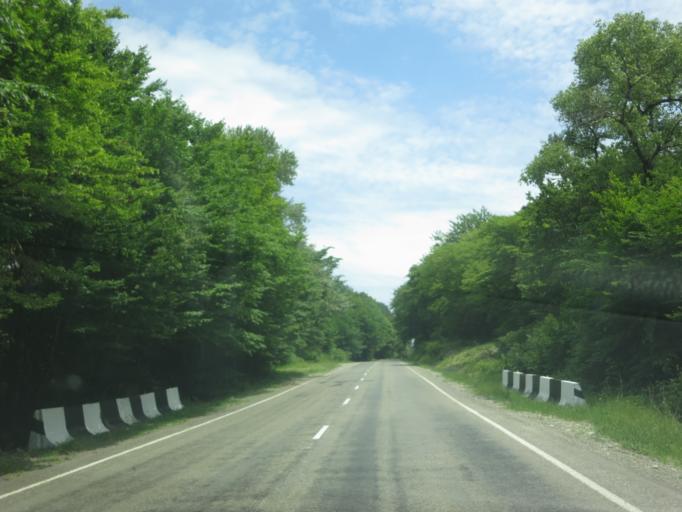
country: GE
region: Kakheti
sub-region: Telavi
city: Telavi
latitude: 41.9080
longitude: 45.3791
